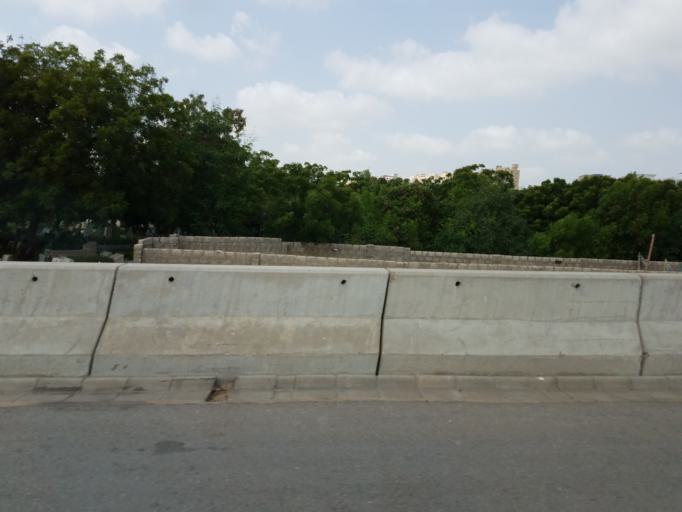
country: PK
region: Sindh
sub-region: Karachi District
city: Karachi
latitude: 24.9147
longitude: 67.0777
